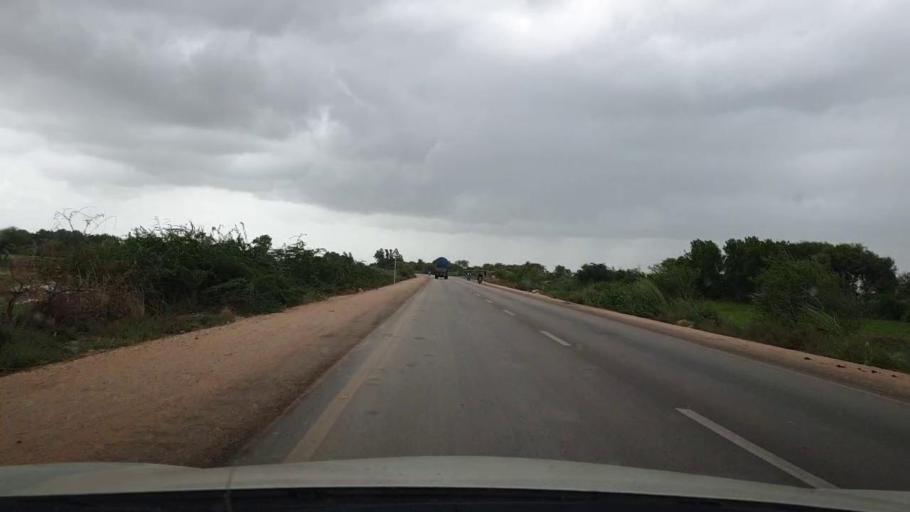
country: PK
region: Sindh
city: Kario
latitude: 24.6426
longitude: 68.4632
